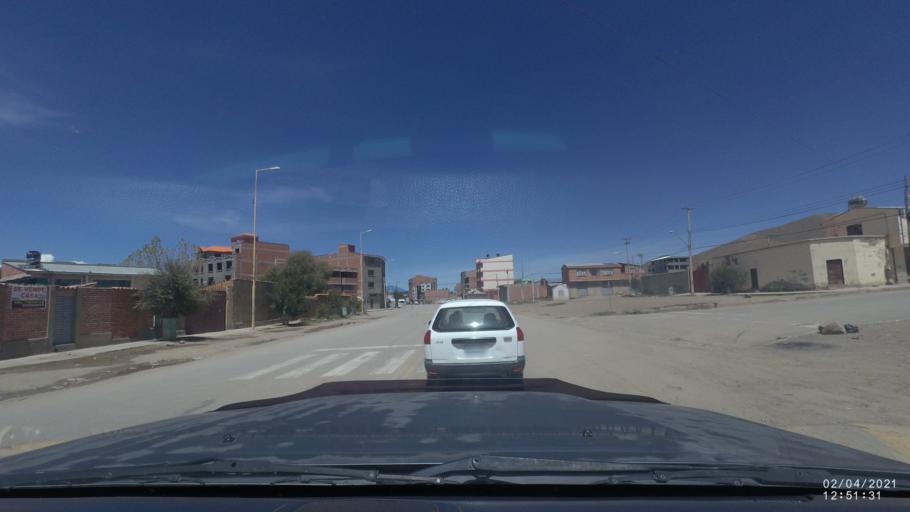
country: BO
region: Oruro
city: Oruro
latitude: -17.9826
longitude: -67.1367
